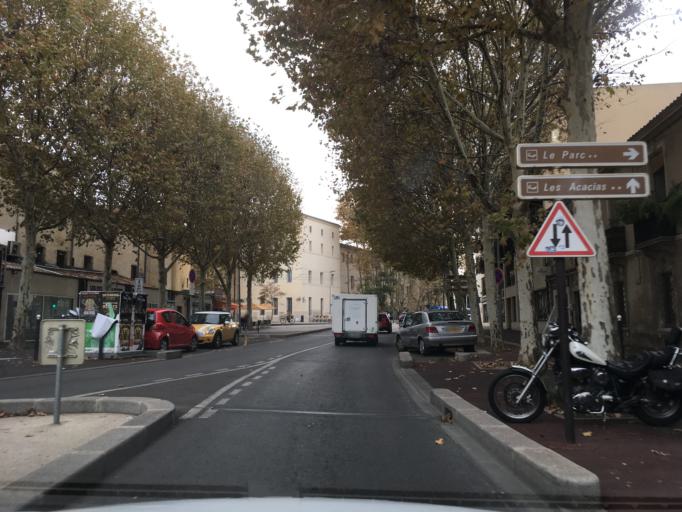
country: FR
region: Languedoc-Roussillon
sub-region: Departement de l'Herault
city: Montpellier
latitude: 43.6160
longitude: 3.8755
